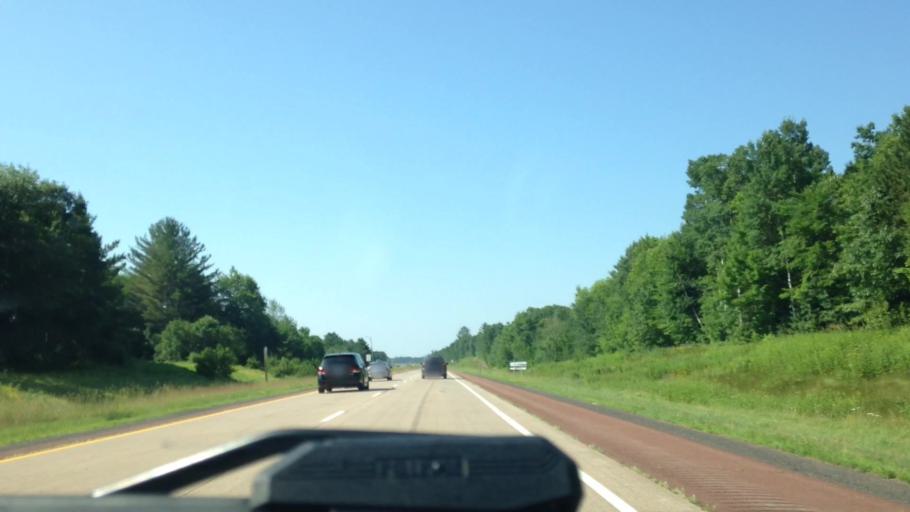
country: US
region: Wisconsin
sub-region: Douglas County
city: Lake Nebagamon
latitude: 46.3843
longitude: -91.8220
